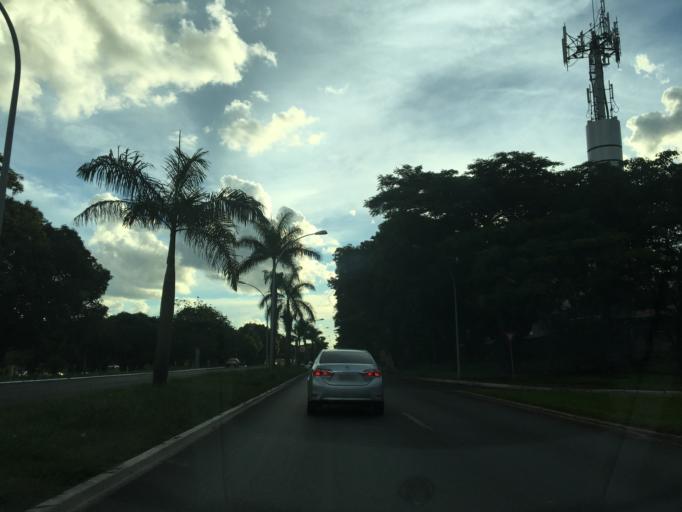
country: BR
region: Federal District
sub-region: Brasilia
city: Brasilia
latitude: -15.8128
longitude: -47.8966
